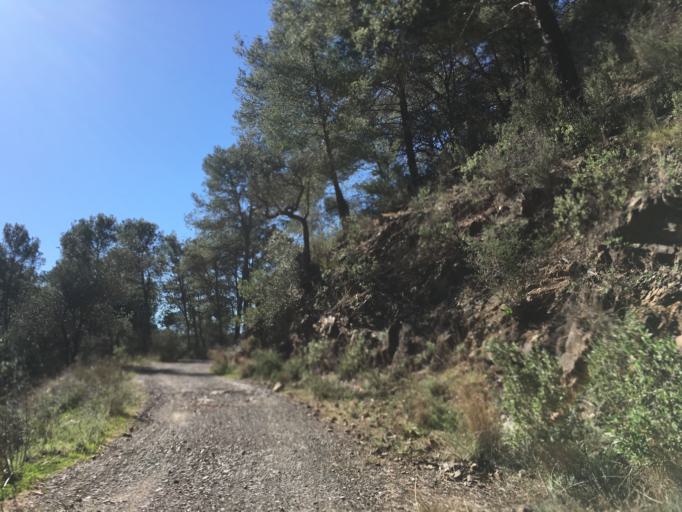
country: ES
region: Andalusia
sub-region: Provincia de Malaga
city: Malaga
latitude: 36.8060
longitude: -4.3989
